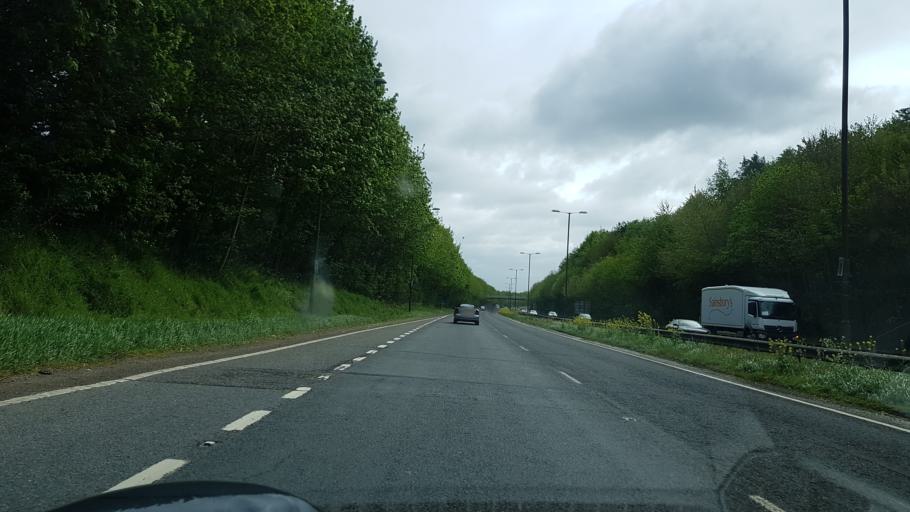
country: GB
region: England
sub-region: Hampshire
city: Basingstoke
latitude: 51.2785
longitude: -1.0954
